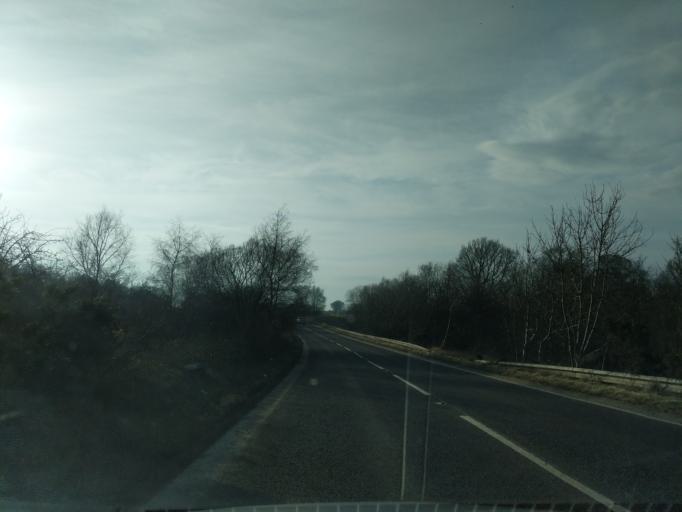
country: GB
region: Scotland
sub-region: South Lanarkshire
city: Law
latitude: 55.7359
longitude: -3.8702
